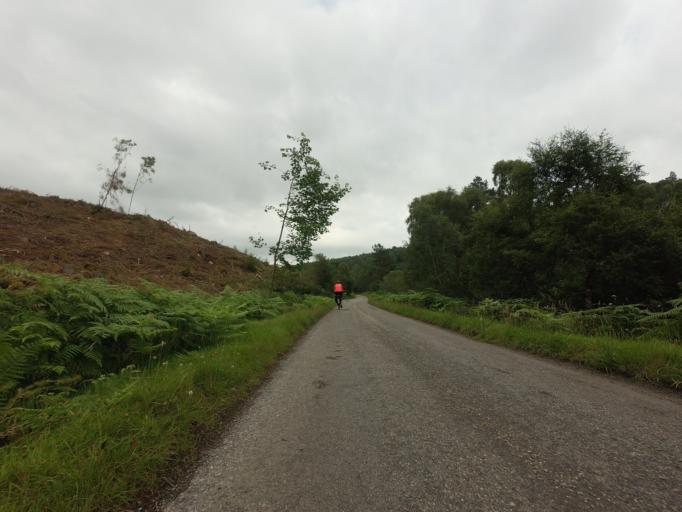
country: GB
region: Scotland
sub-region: Highland
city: Evanton
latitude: 57.9464
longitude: -4.4070
